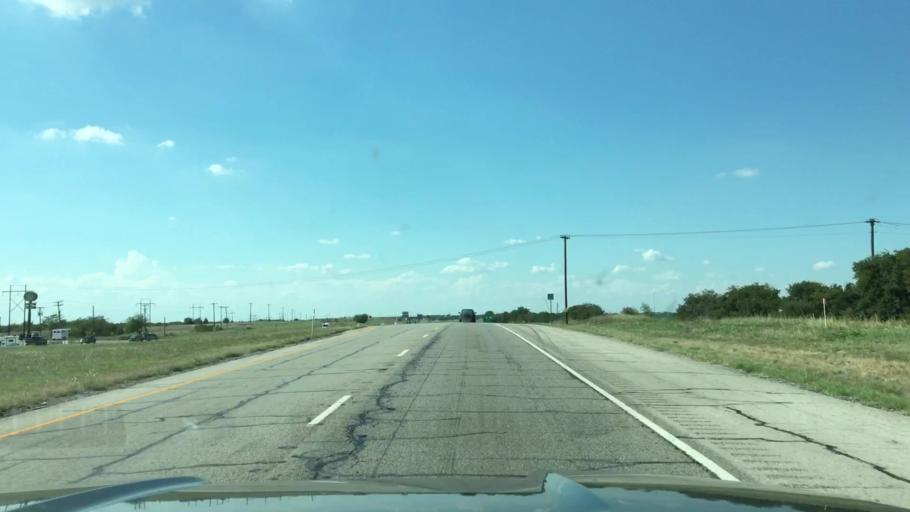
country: US
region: Texas
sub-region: Wise County
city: Decatur
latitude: 33.1787
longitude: -97.5460
